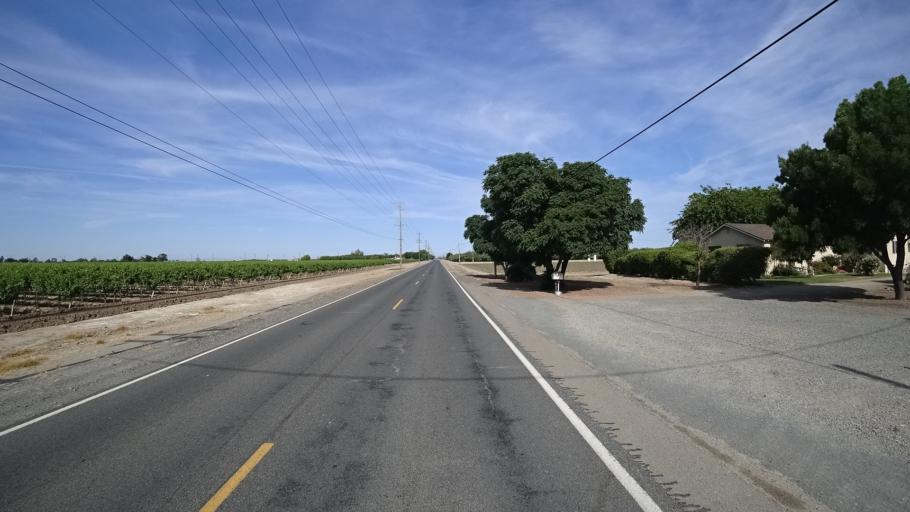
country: US
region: California
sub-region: Kings County
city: Hanford
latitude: 36.3427
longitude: -119.5766
